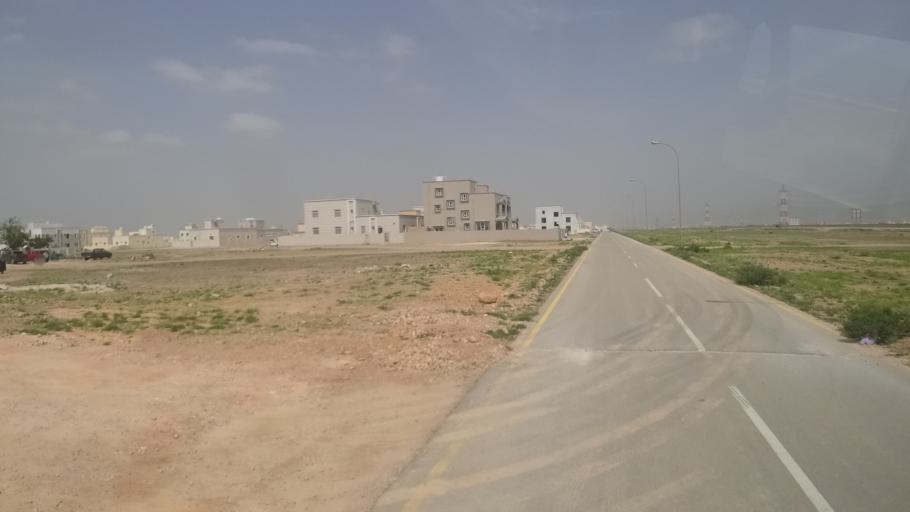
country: OM
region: Zufar
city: Salalah
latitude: 17.1027
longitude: 54.2139
